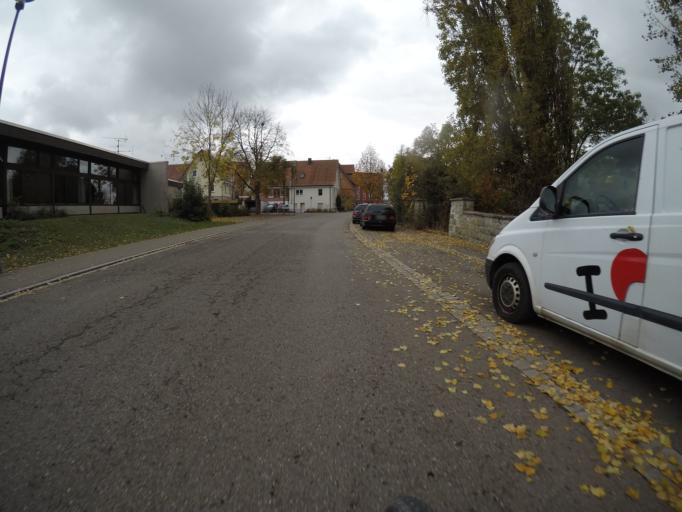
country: DE
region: Baden-Wuerttemberg
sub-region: Regierungsbezirk Stuttgart
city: Ehningen
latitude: 48.6570
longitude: 8.9449
